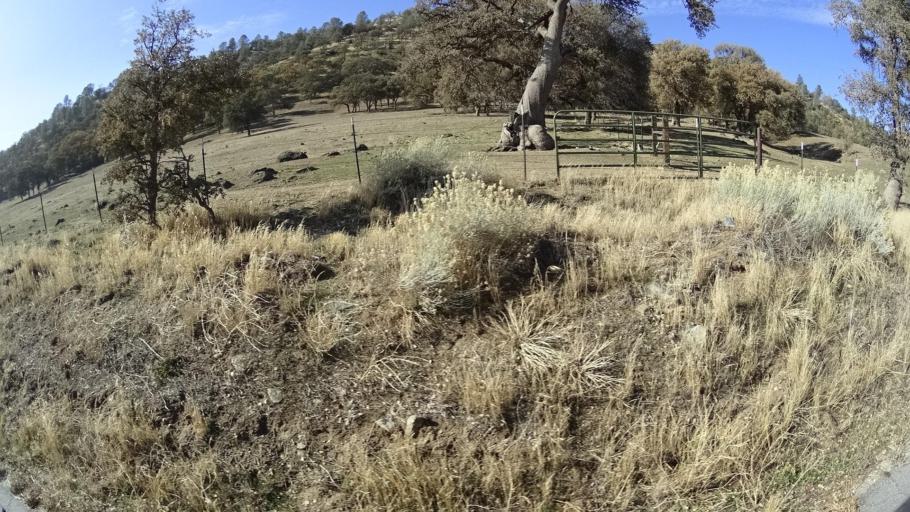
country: US
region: California
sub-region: Kern County
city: Bodfish
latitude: 35.3930
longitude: -118.5493
